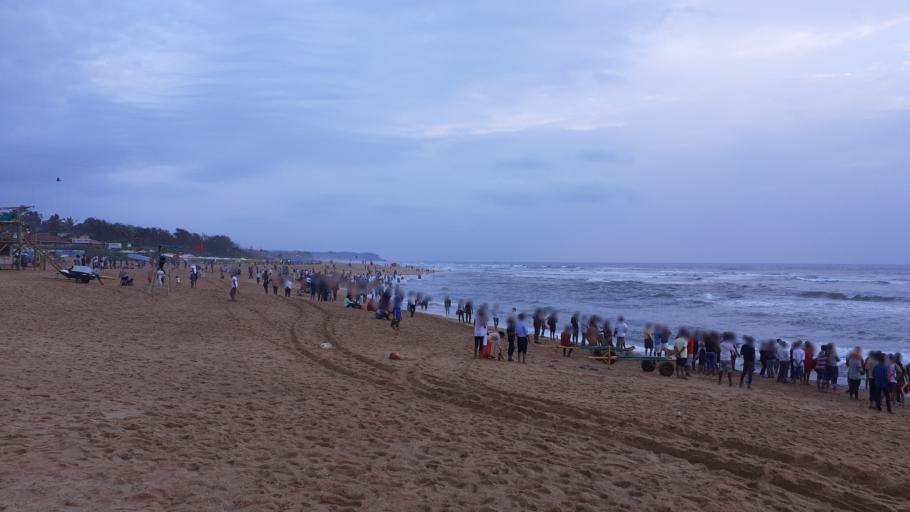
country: IN
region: Goa
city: Calangute
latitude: 15.5459
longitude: 73.7546
